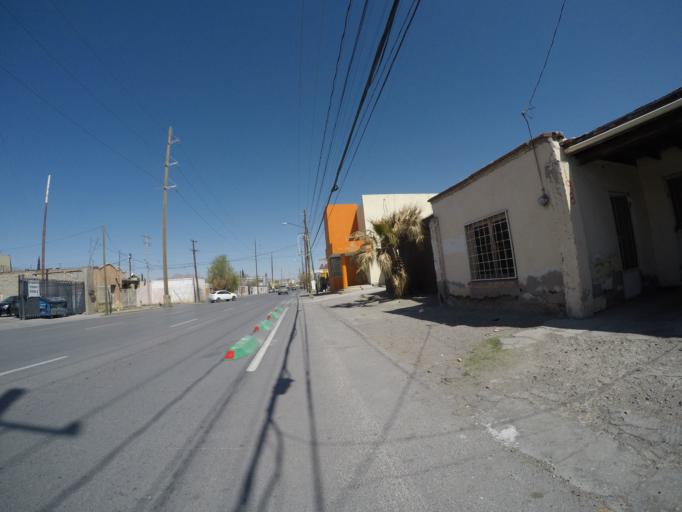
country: MX
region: Chihuahua
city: Ciudad Juarez
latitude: 31.7359
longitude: -106.4406
